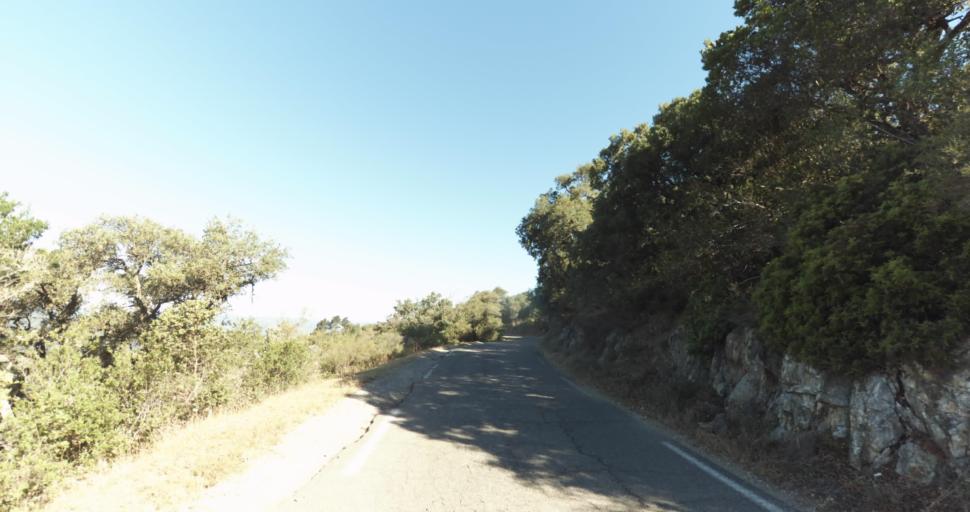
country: FR
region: Provence-Alpes-Cote d'Azur
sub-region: Departement du Var
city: Ramatuelle
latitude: 43.2162
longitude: 6.6014
